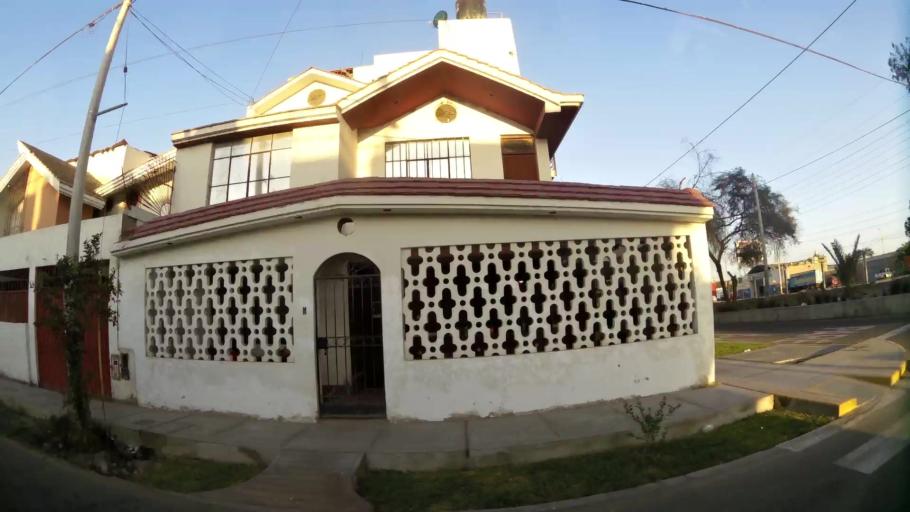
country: PE
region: Ica
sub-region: Provincia de Ica
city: Ica
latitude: -14.0875
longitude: -75.7255
